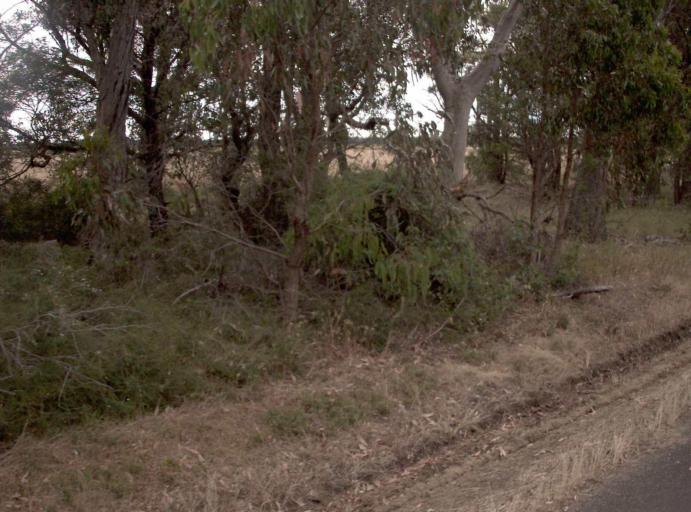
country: AU
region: Victoria
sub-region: Wellington
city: Sale
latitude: -38.3663
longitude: 146.9892
